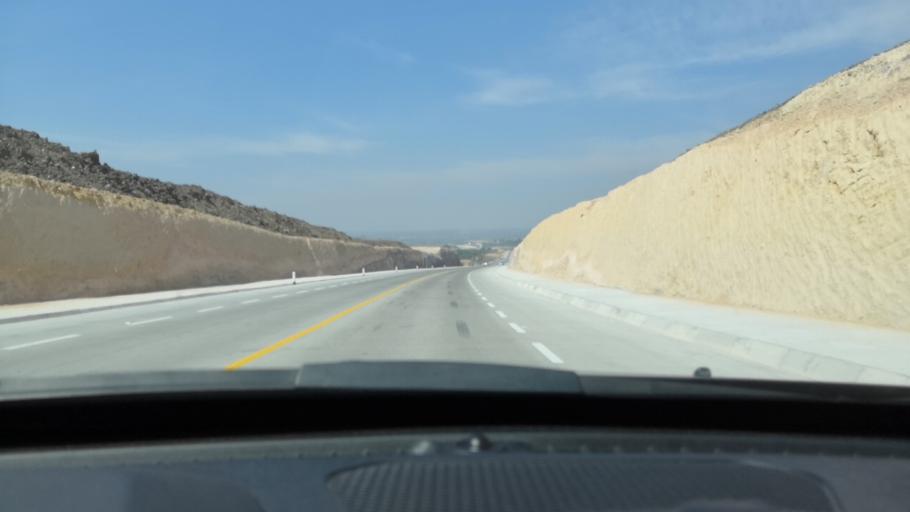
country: MX
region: Guanajuato
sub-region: San Francisco del Rincon
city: Estacion de San Francisco
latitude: 21.0870
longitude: -101.8011
